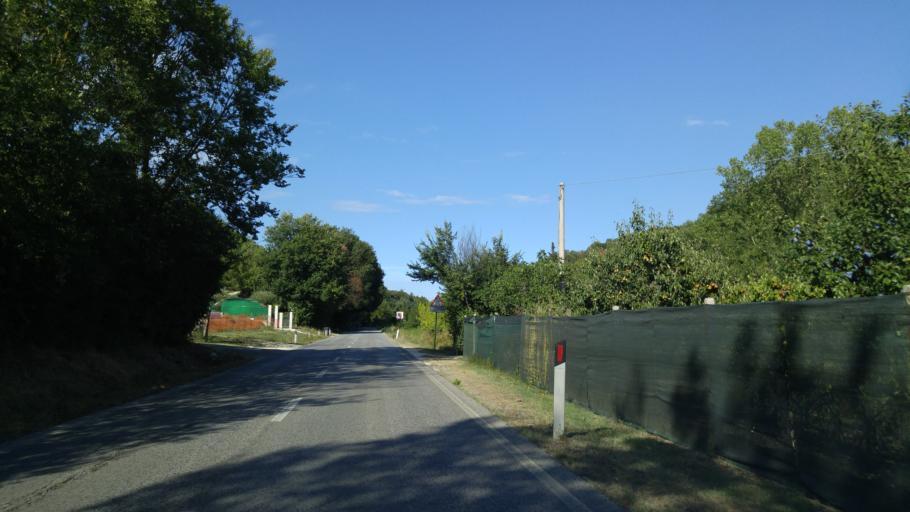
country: IT
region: The Marches
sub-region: Provincia di Pesaro e Urbino
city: Villa Ceccolini
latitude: 43.8622
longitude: 12.8729
